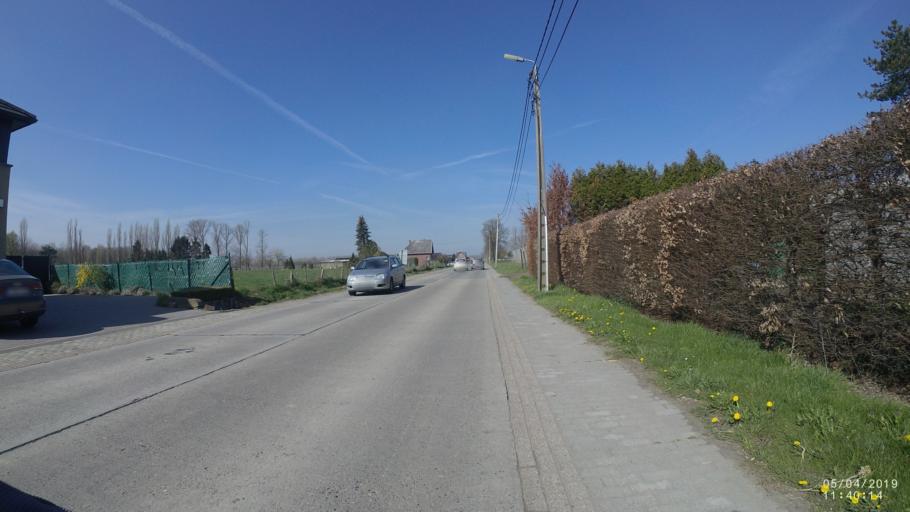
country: BE
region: Flanders
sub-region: Provincie Limburg
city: Herk-de-Stad
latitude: 50.8954
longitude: 5.1580
